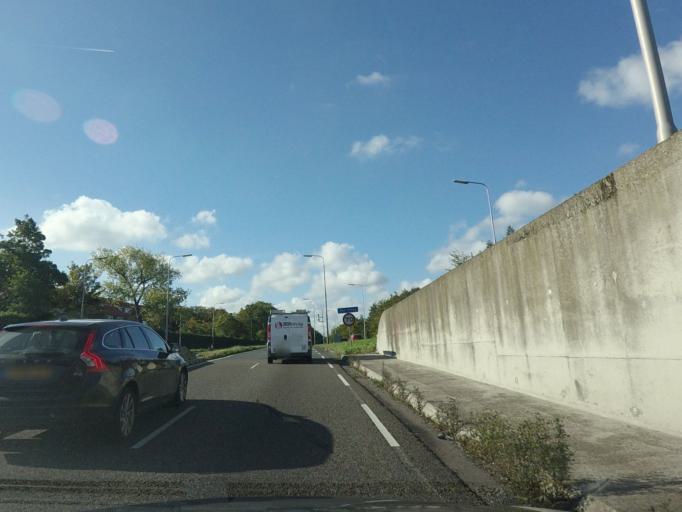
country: NL
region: South Holland
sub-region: Gemeente Leidschendam-Voorburg
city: Voorburg
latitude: 52.1046
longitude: 4.3568
